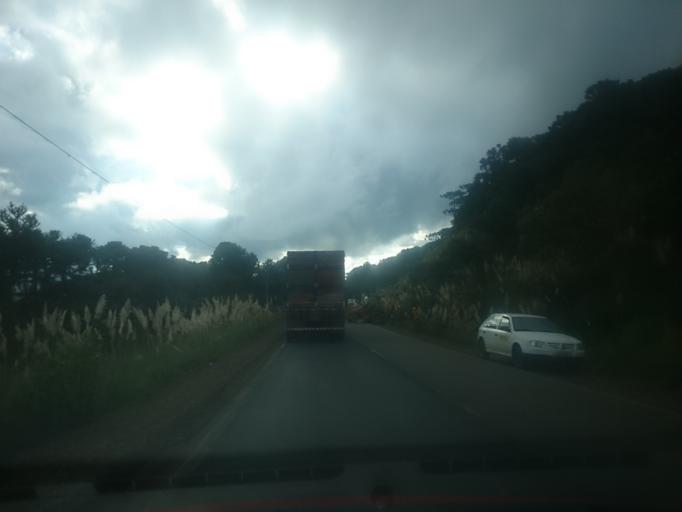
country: BR
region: Santa Catarina
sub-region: Sao Joaquim
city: Sao Joaquim
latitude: -28.3308
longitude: -49.7035
